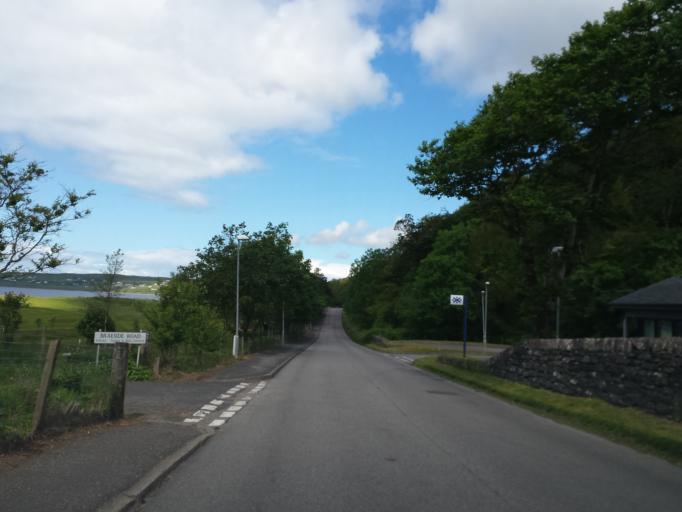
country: GB
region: Scotland
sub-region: Highland
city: Ullapool
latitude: 57.7143
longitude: -5.6810
